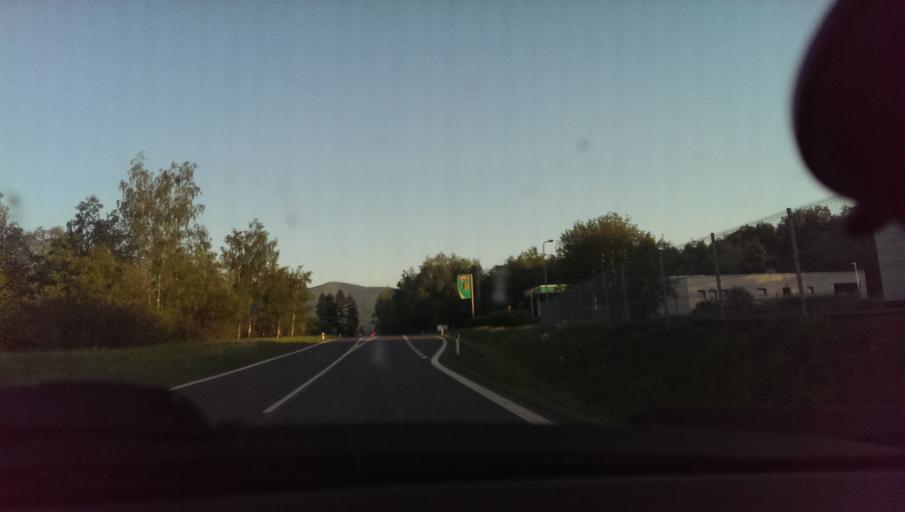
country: CZ
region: Moravskoslezsky
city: Frenstat pod Radhostem
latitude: 49.5564
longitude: 18.1991
